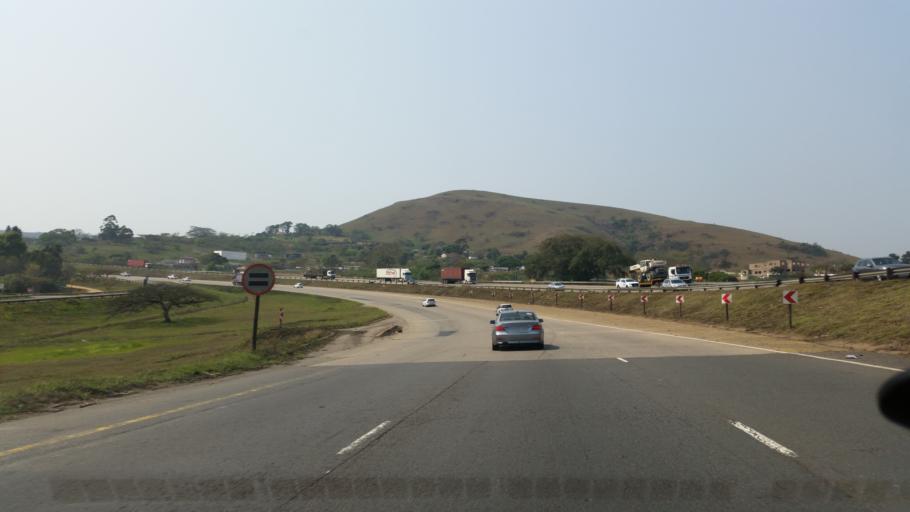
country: ZA
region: KwaZulu-Natal
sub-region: eThekwini Metropolitan Municipality
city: Mpumalanga
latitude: -29.7710
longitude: 30.6847
